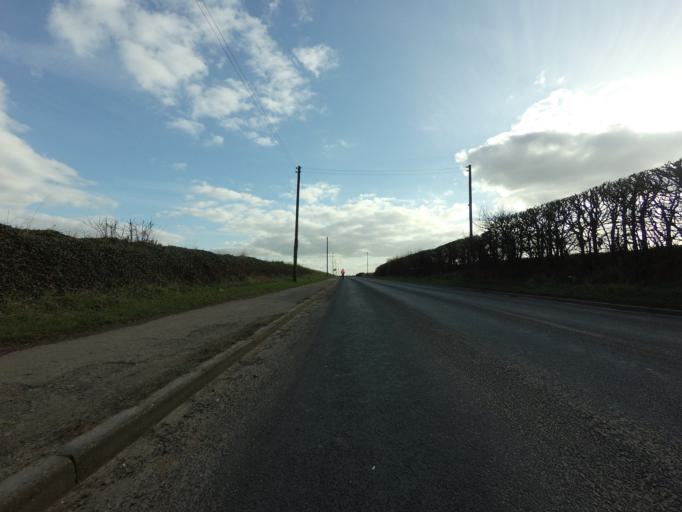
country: GB
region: England
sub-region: Kent
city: Dartford
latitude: 51.4196
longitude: 0.2019
